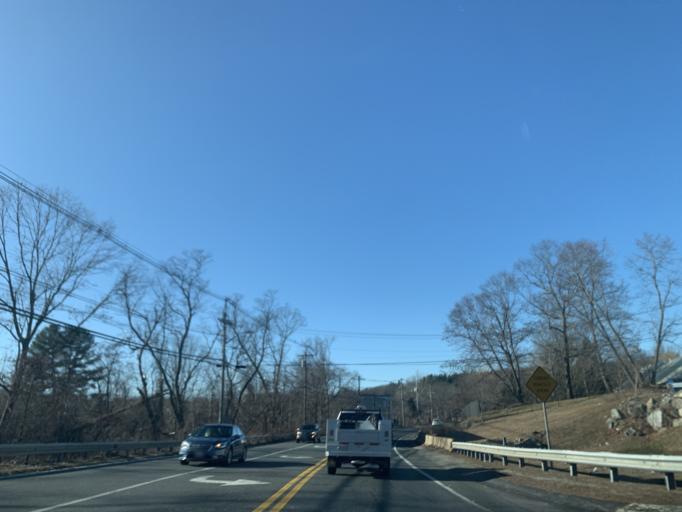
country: US
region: Massachusetts
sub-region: Middlesex County
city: Marlborough
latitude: 42.3477
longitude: -71.5137
